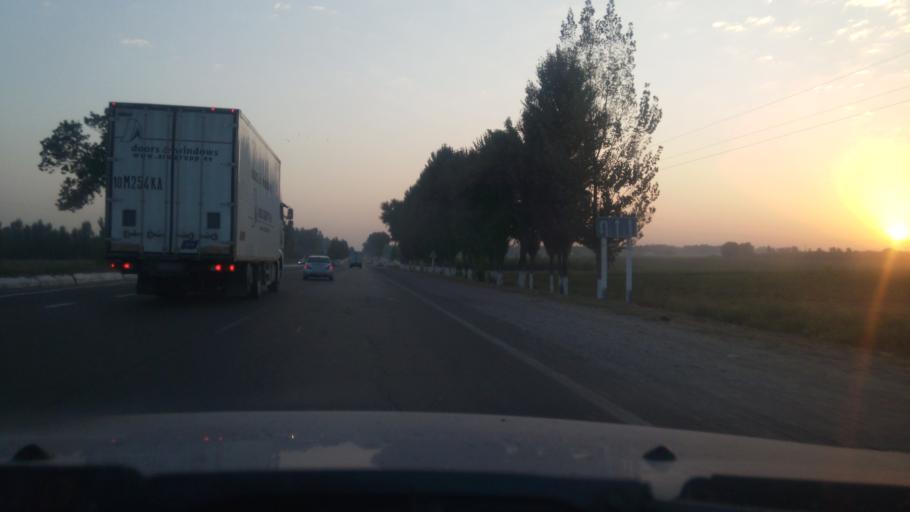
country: UZ
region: Toshkent
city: Zafar
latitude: 41.0337
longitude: 68.8716
